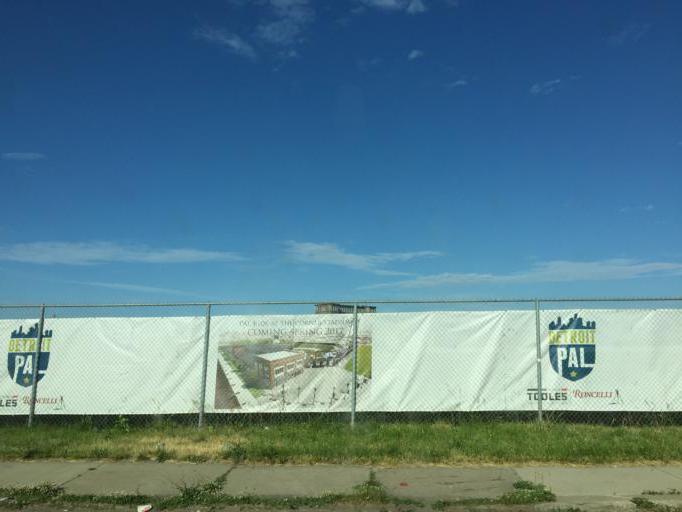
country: US
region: Michigan
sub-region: Wayne County
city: Detroit
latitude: 42.3326
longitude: -83.0676
